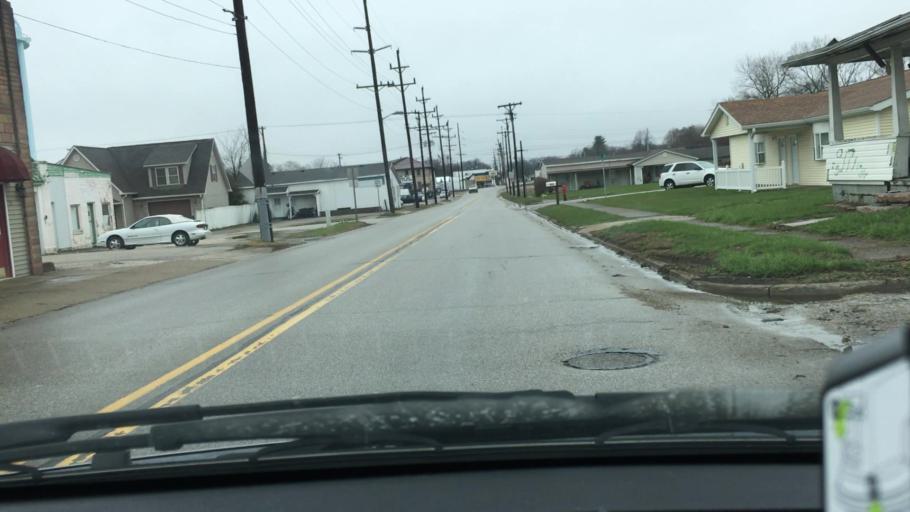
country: US
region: Indiana
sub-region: Lawrence County
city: Bedford
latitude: 38.8743
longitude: -86.4835
